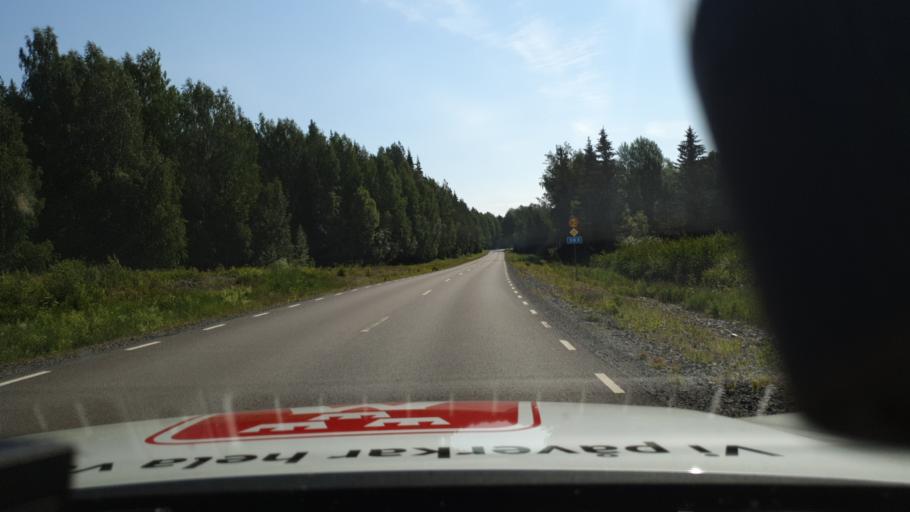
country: SE
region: Norrbotten
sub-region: Lulea Kommun
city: Sodra Sunderbyn
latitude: 65.8322
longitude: 21.9552
